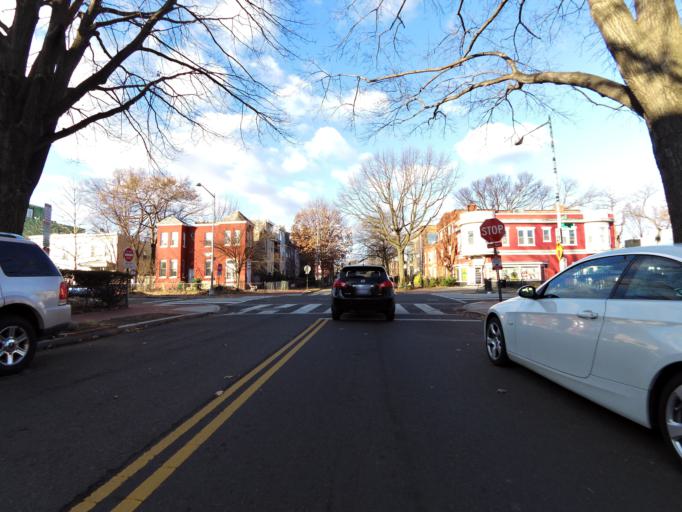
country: US
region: Washington, D.C.
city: Washington, D.C.
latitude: 38.9096
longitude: -77.0149
